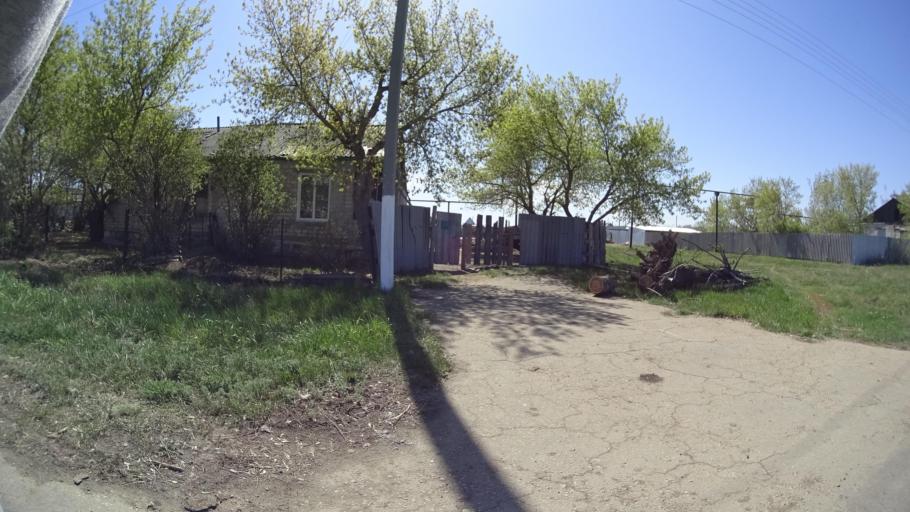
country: RU
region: Chelyabinsk
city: Chesma
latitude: 53.7912
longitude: 61.0397
